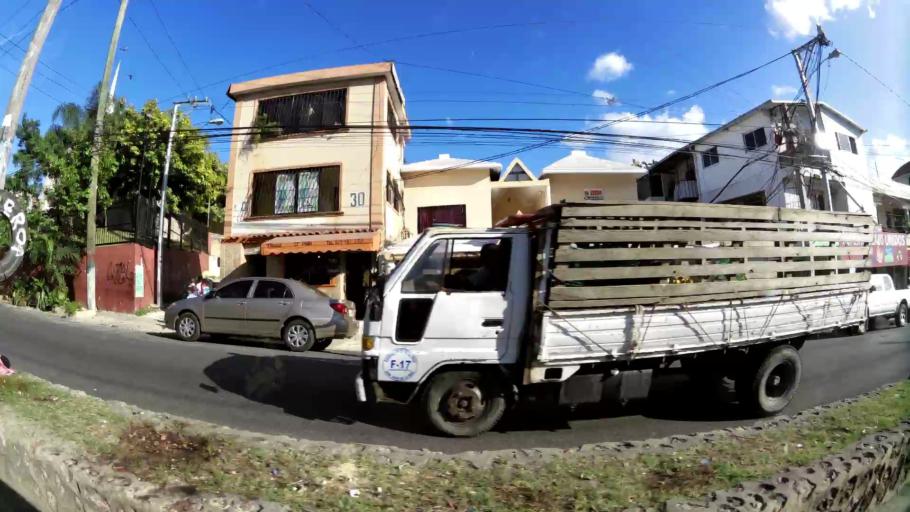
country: DO
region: Nacional
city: Santo Domingo
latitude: 18.5002
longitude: -69.9618
